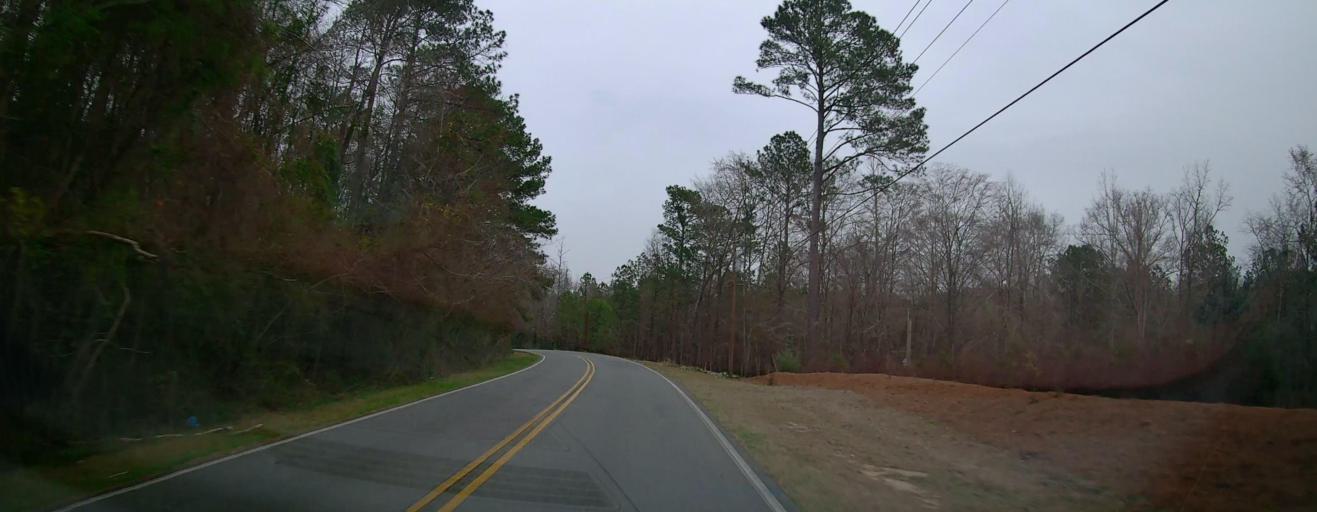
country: US
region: Georgia
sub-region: Bibb County
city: Macon
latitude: 32.8582
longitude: -83.7102
